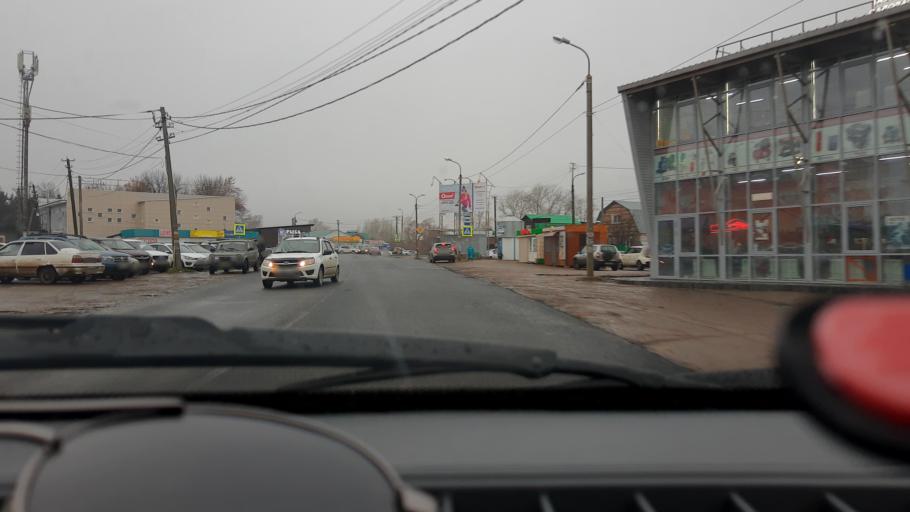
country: RU
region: Bashkortostan
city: Kabakovo
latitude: 54.6232
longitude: 56.1109
